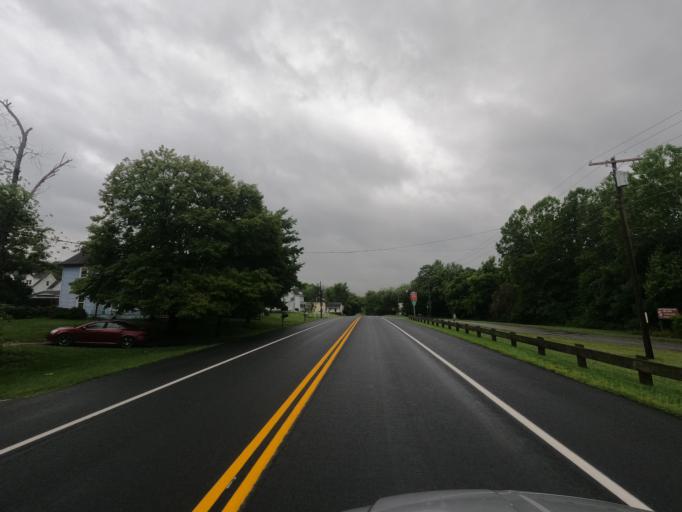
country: US
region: West Virginia
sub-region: Berkeley County
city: Martinsburg
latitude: 39.6241
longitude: -78.0167
